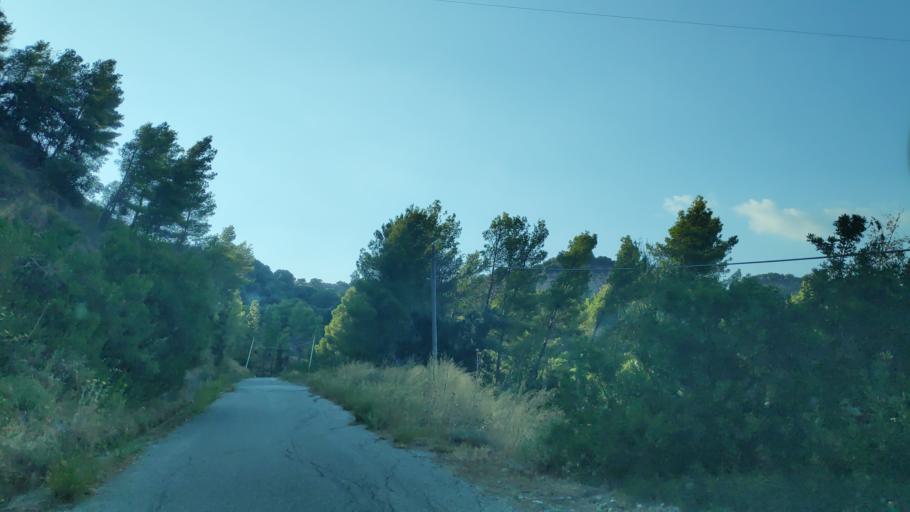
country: IT
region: Calabria
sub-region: Provincia di Reggio Calabria
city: Placanica
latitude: 38.4099
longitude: 16.4317
